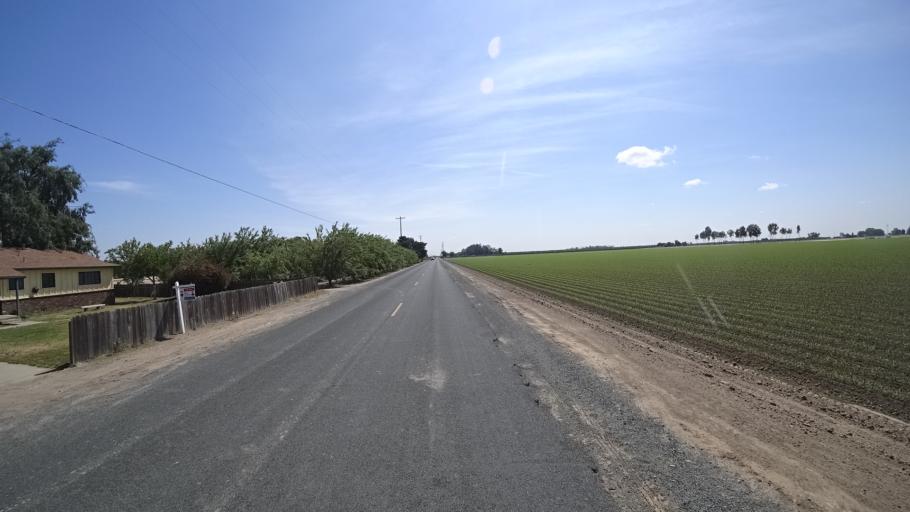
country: US
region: California
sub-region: Kings County
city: Armona
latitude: 36.2692
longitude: -119.7207
